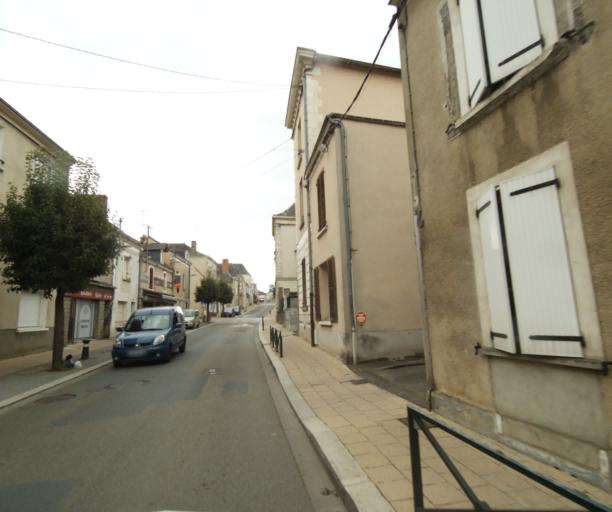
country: FR
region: Pays de la Loire
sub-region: Departement de la Sarthe
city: Sable-sur-Sarthe
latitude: 47.8381
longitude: -0.3265
